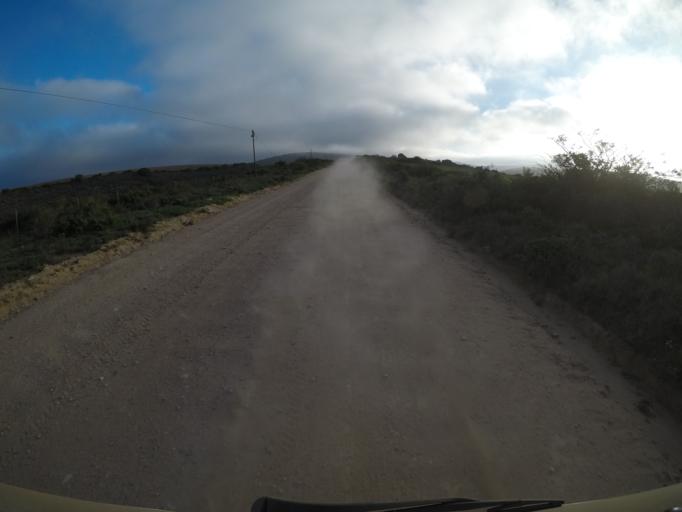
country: ZA
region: Western Cape
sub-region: Eden District Municipality
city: Mossel Bay
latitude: -34.1329
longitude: 22.0444
